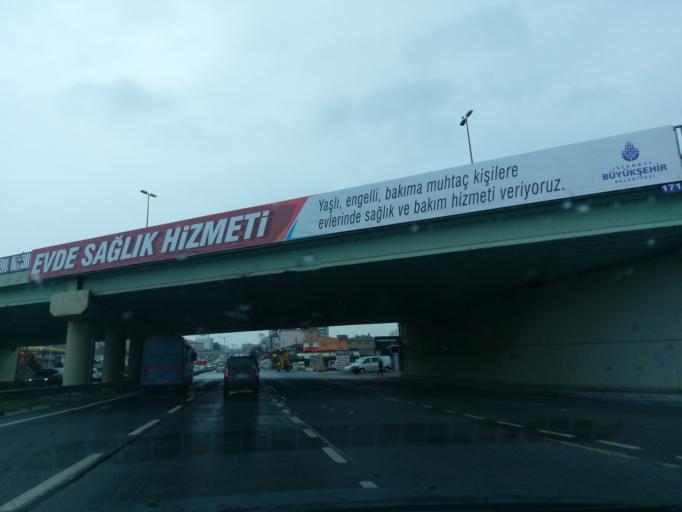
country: TR
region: Istanbul
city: Mimarsinan
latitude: 41.0183
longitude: 28.5637
